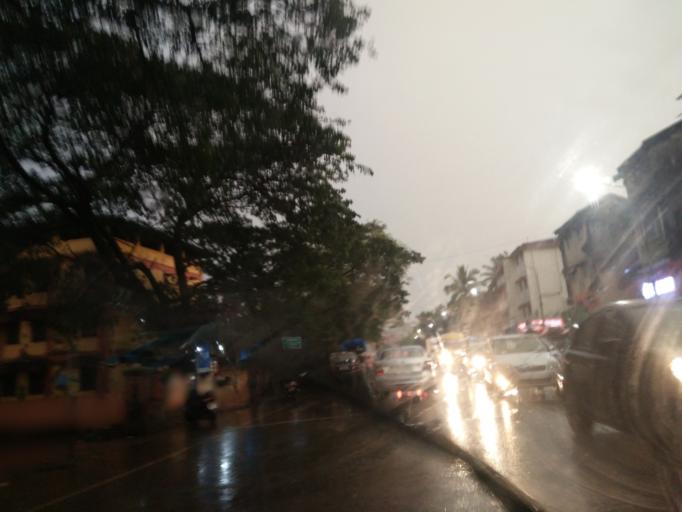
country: IN
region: Goa
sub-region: South Goa
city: Madgaon
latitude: 15.2845
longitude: 73.9749
